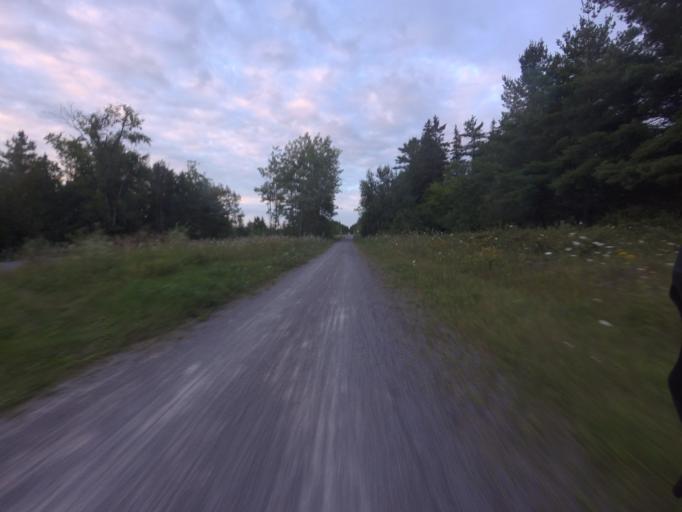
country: CA
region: Ontario
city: Bells Corners
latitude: 45.2188
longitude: -75.9832
